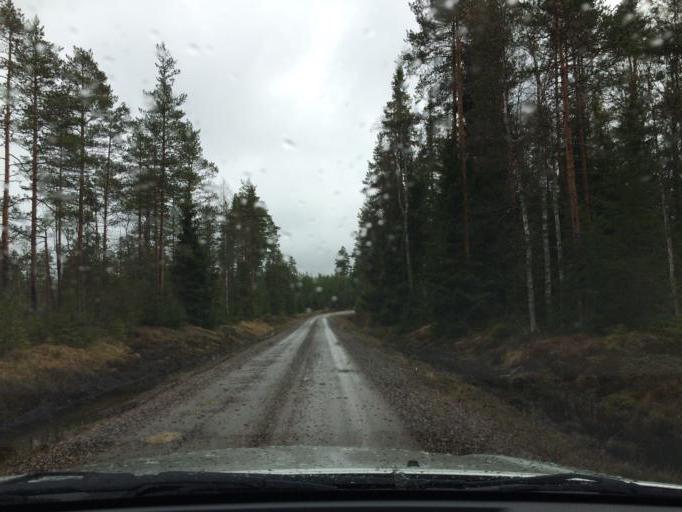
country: SE
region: OErebro
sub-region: Hallefors Kommun
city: Haellefors
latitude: 60.0288
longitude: 14.5554
